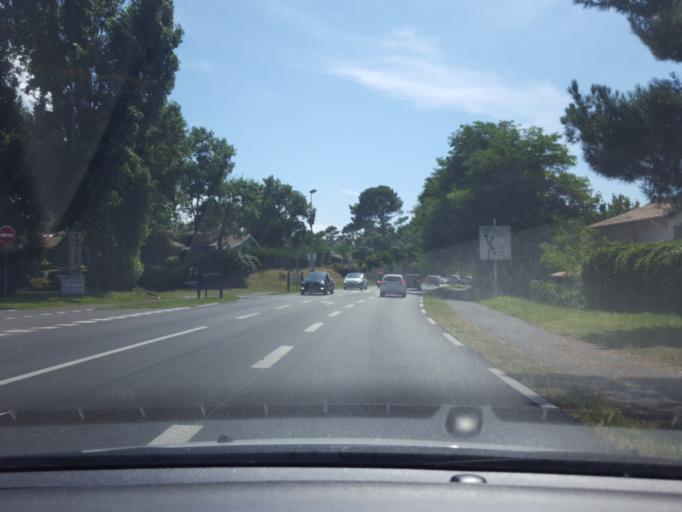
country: FR
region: Aquitaine
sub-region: Departement des Landes
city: Capbreton
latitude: 43.6325
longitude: -1.4284
